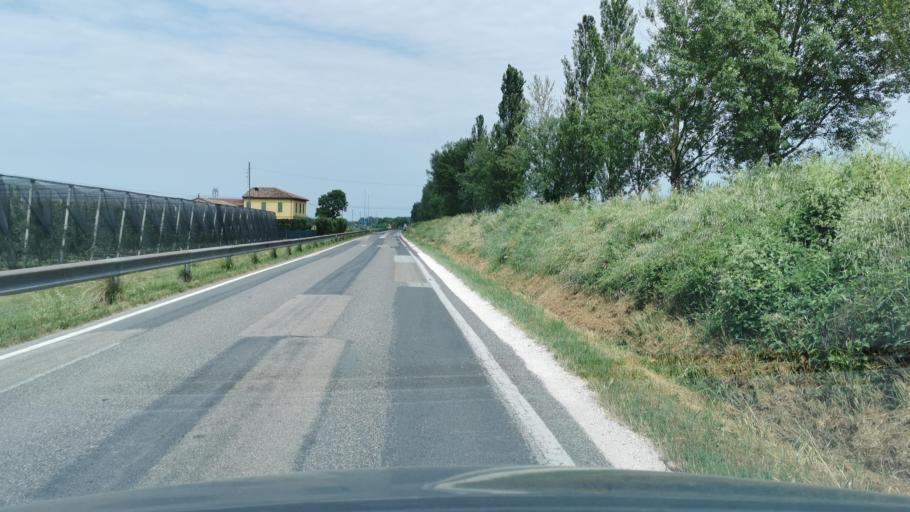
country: IT
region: Emilia-Romagna
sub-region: Provincia di Ravenna
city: Alfonsine
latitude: 44.4775
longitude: 12.0357
